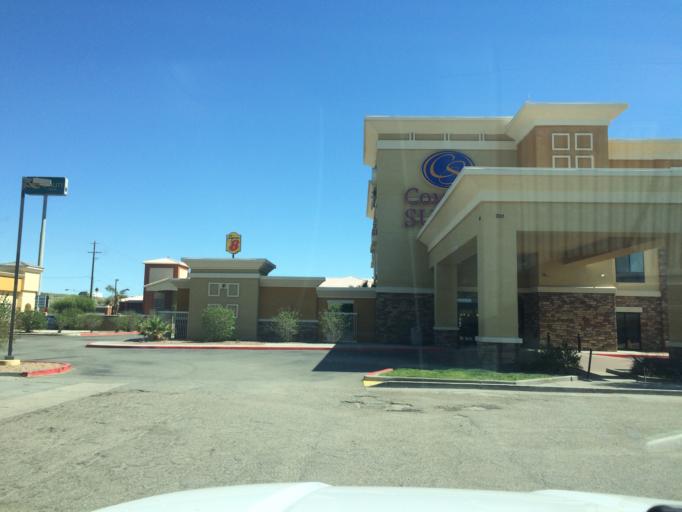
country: US
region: California
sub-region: Riverside County
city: Blythe
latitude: 33.6060
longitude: -114.6049
